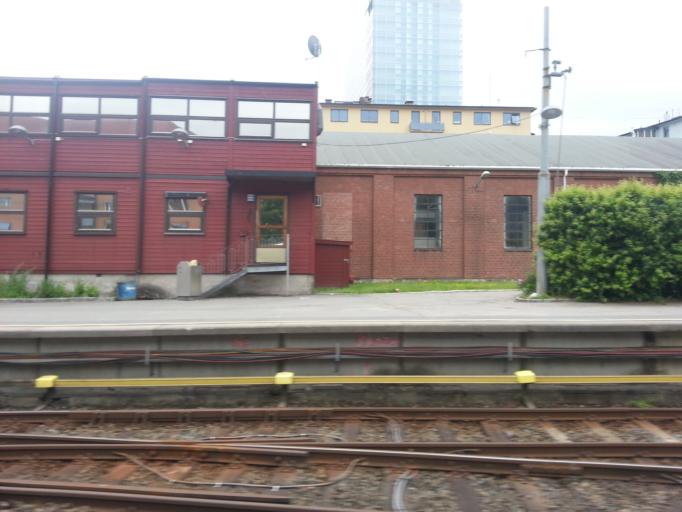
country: NO
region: Oslo
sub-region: Oslo
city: Sjolyststranda
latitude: 59.9307
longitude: 10.7140
